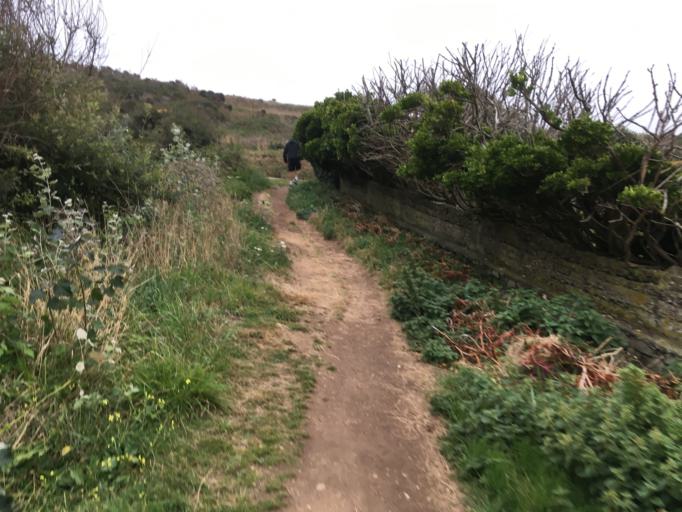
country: FR
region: Brittany
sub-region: Departement du Finistere
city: Plogoff
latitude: 48.0497
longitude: -4.7051
